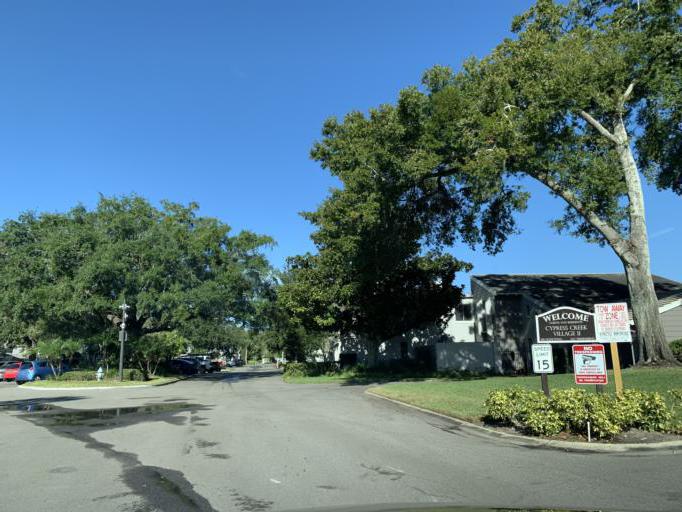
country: US
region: Florida
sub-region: Orange County
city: Oak Ridge
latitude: 28.4866
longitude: -81.4484
